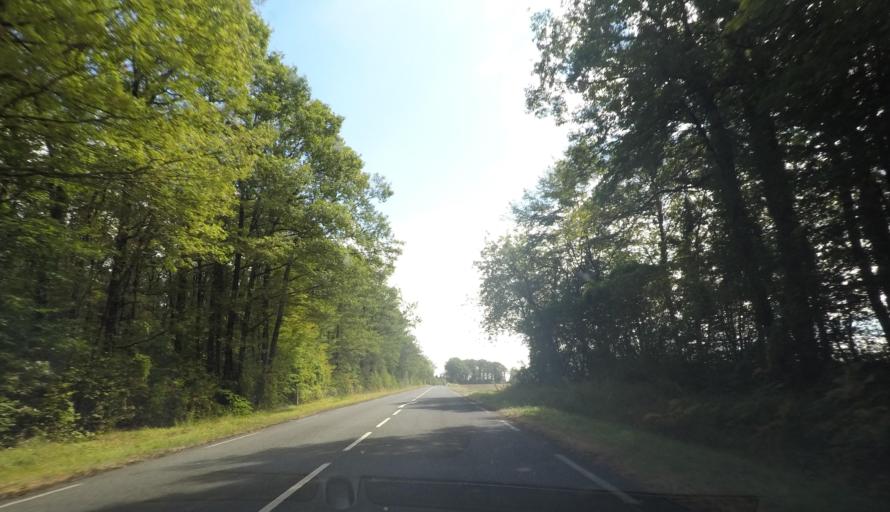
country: FR
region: Pays de la Loire
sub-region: Departement de la Sarthe
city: Saint-Cosme-en-Vairais
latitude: 48.2688
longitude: 0.4957
